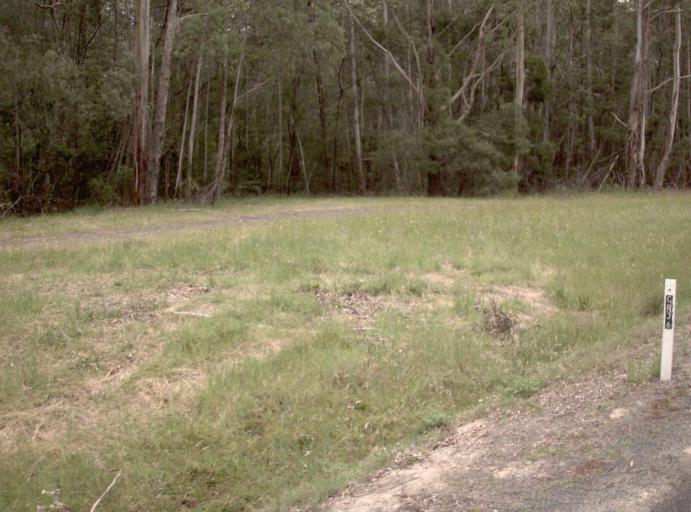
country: AU
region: New South Wales
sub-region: Bombala
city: Bombala
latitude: -37.2826
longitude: 149.2225
